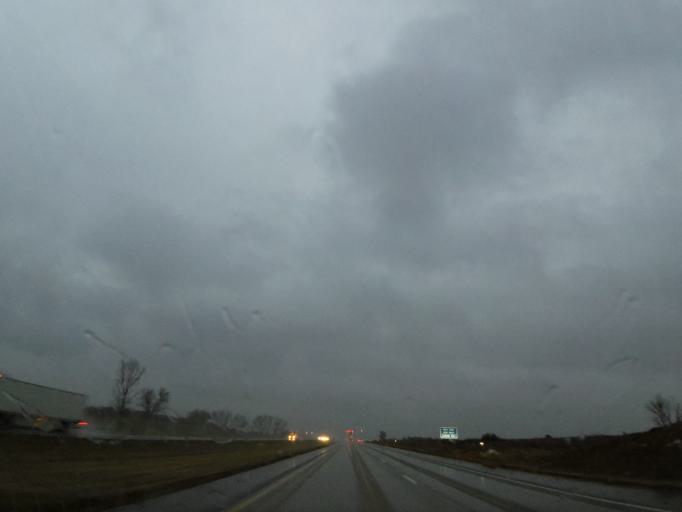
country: US
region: Iowa
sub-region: Worth County
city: Northwood
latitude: 43.3944
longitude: -93.3494
